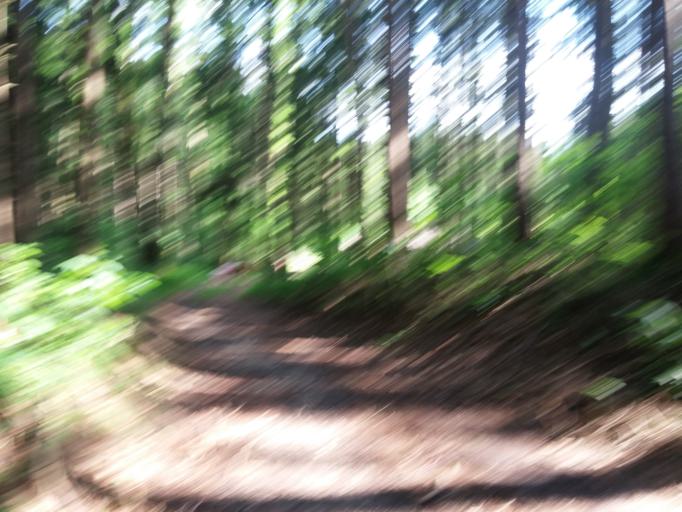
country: DE
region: Bavaria
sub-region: Swabia
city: Woringen
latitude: 47.8775
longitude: 10.1997
